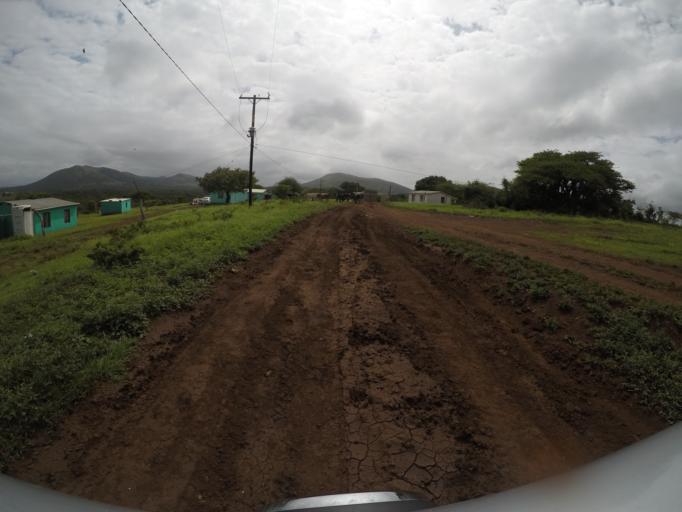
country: ZA
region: KwaZulu-Natal
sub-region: uThungulu District Municipality
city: Empangeni
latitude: -28.6202
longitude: 31.8725
